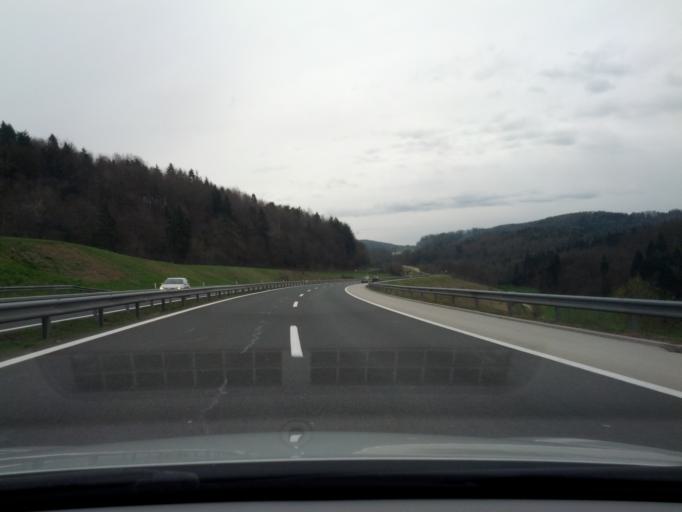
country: SI
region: Ivancna Gorica
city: Sentvid pri Sticni
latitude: 45.9295
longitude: 14.9266
